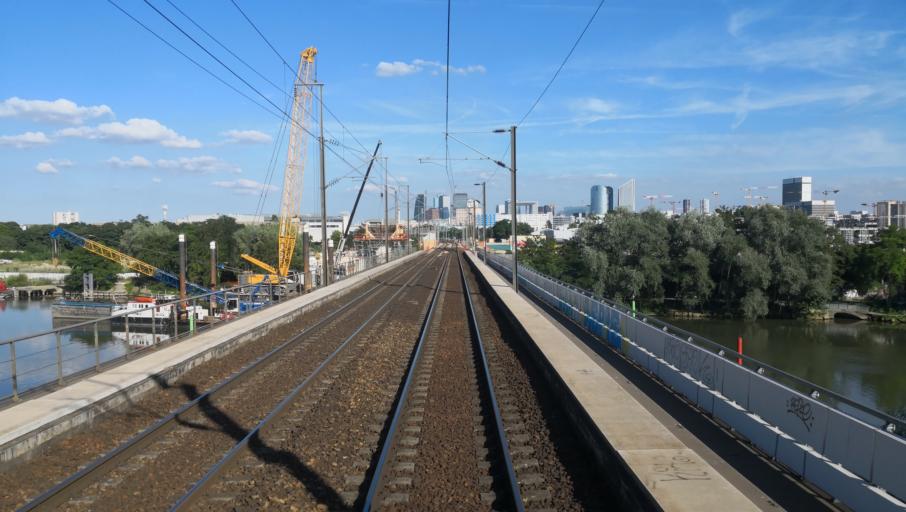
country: FR
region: Ile-de-France
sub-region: Departement du Val-d'Oise
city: Bezons
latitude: 48.9110
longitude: 2.2046
